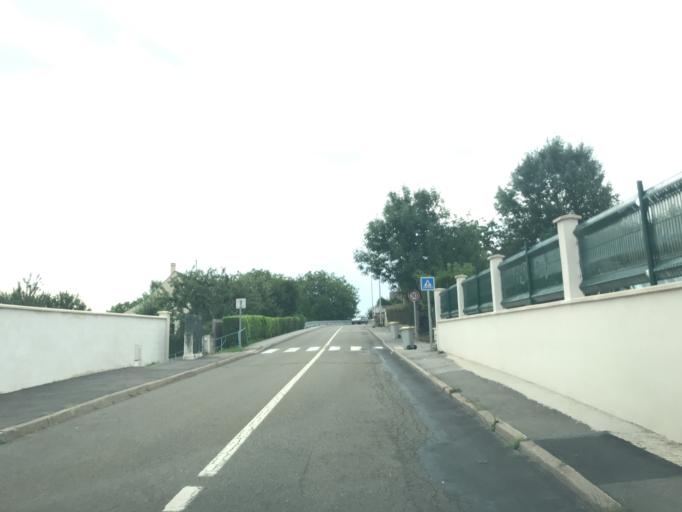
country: FR
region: Ile-de-France
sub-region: Departement des Yvelines
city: Elancourt
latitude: 48.7821
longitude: 1.9583
